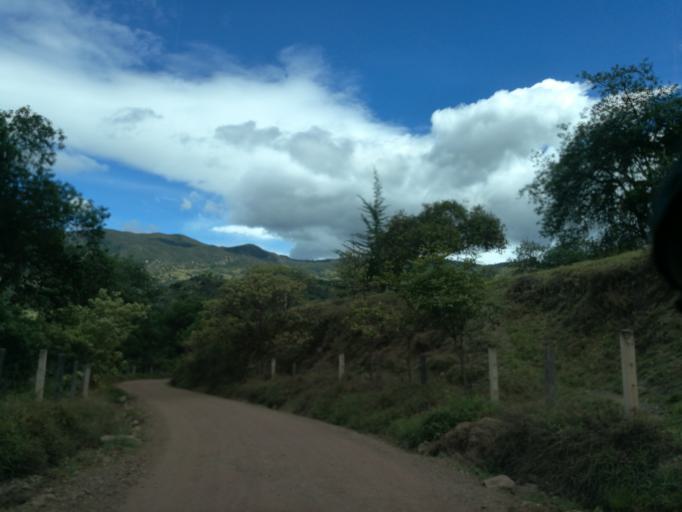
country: CO
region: Boyaca
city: Socota
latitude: 6.1166
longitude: -72.7157
